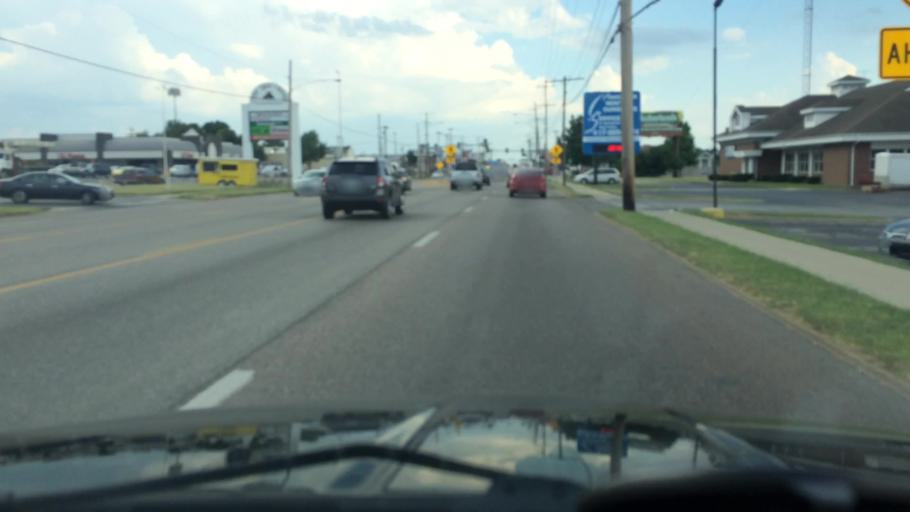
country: US
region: Missouri
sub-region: Greene County
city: Springfield
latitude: 37.1876
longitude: -93.2623
